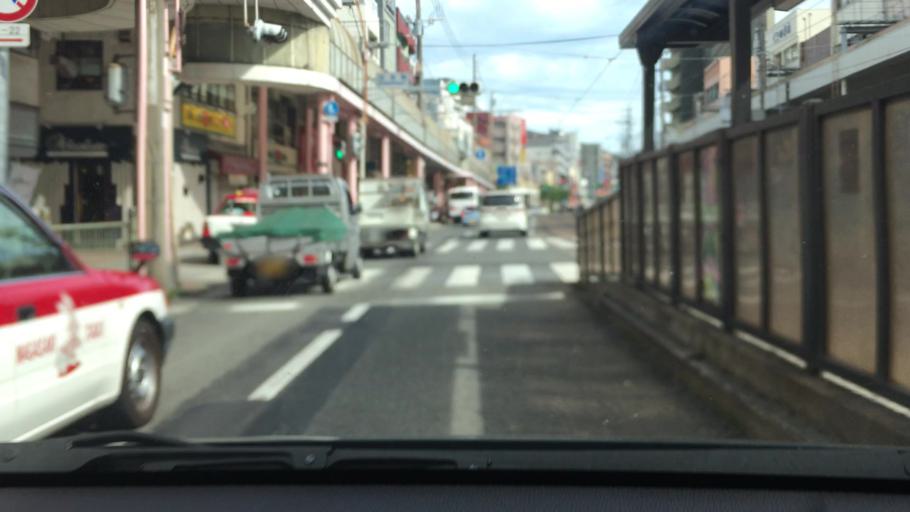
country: JP
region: Nagasaki
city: Obita
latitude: 32.7921
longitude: 129.8599
